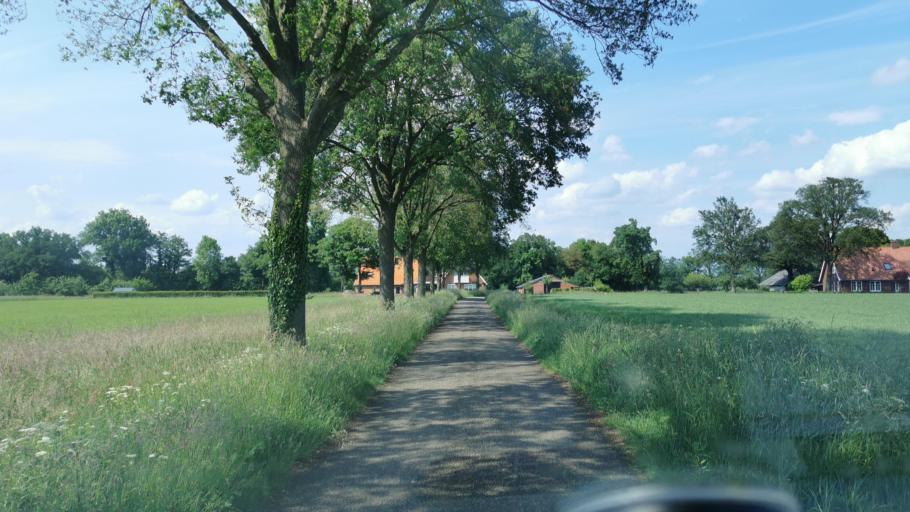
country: NL
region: Overijssel
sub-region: Gemeente Tubbergen
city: Tubbergen
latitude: 52.3449
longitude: 6.8024
